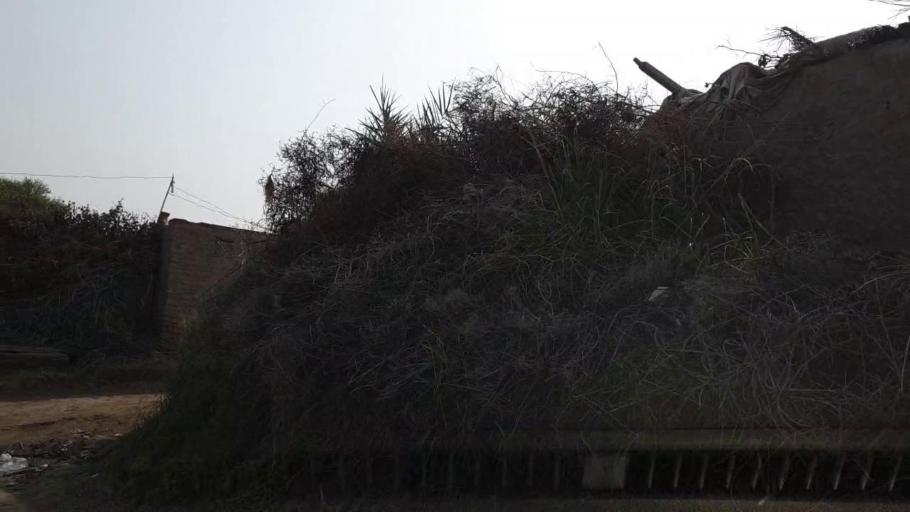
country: PK
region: Sindh
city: Bhan
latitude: 26.4490
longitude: 67.7338
